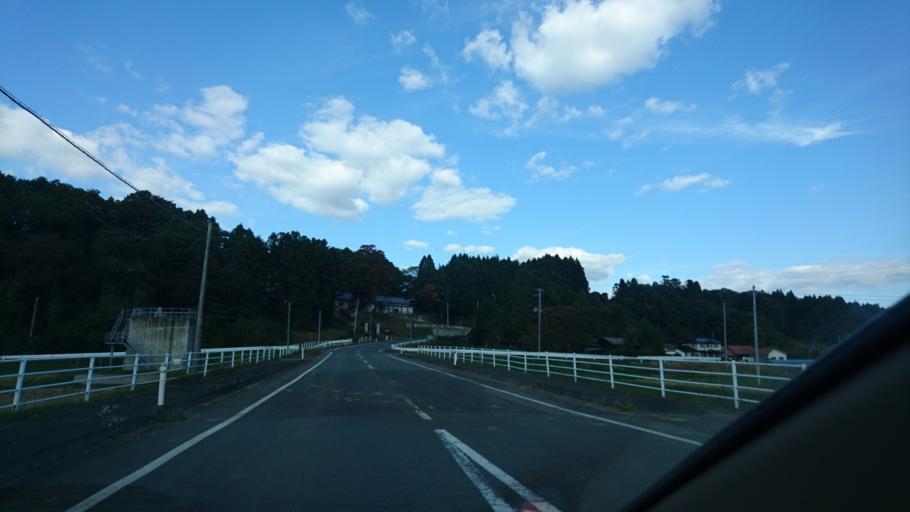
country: JP
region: Iwate
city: Kitakami
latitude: 39.2338
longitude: 141.1250
